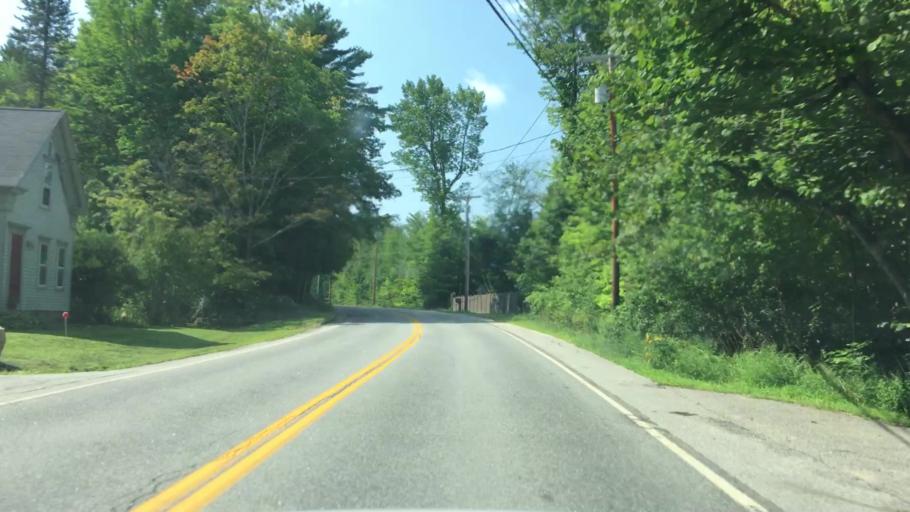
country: US
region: Maine
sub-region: Cumberland County
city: Raymond
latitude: 43.9180
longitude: -70.4372
